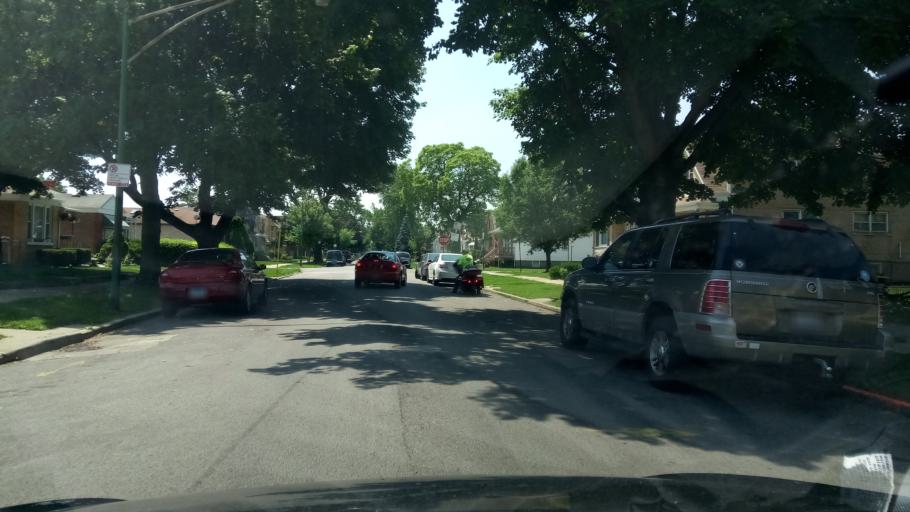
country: US
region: Illinois
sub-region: Cook County
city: Hometown
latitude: 41.7832
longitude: -87.7362
